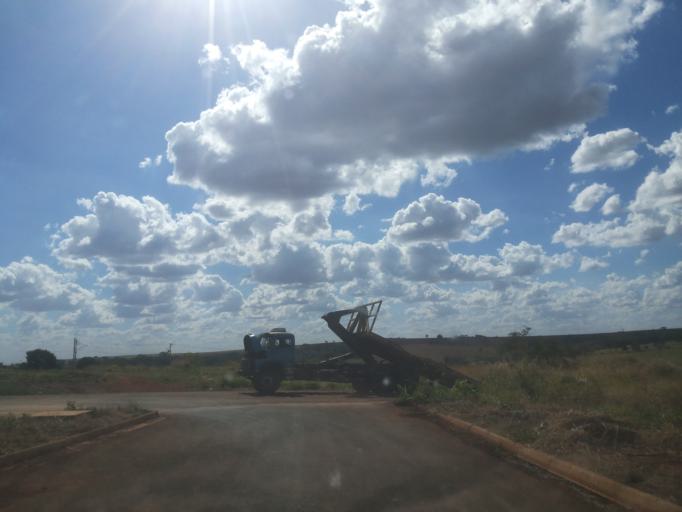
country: BR
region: Minas Gerais
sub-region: Capinopolis
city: Capinopolis
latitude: -18.6842
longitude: -49.5622
